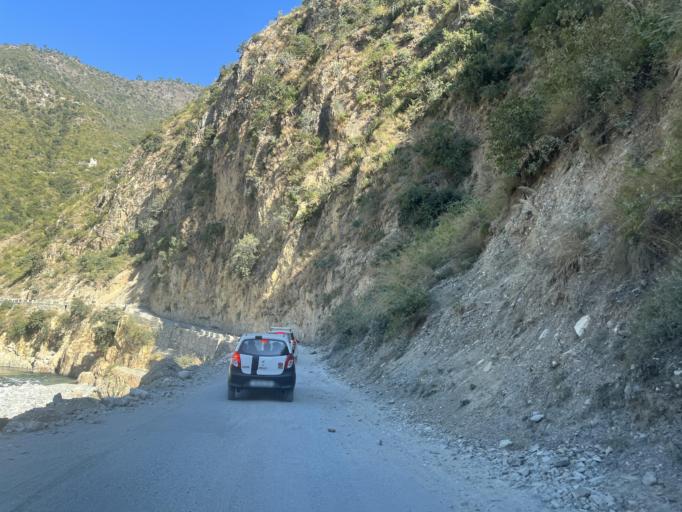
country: IN
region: Uttarakhand
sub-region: Naini Tal
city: Naini Tal
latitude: 29.5072
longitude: 79.4534
